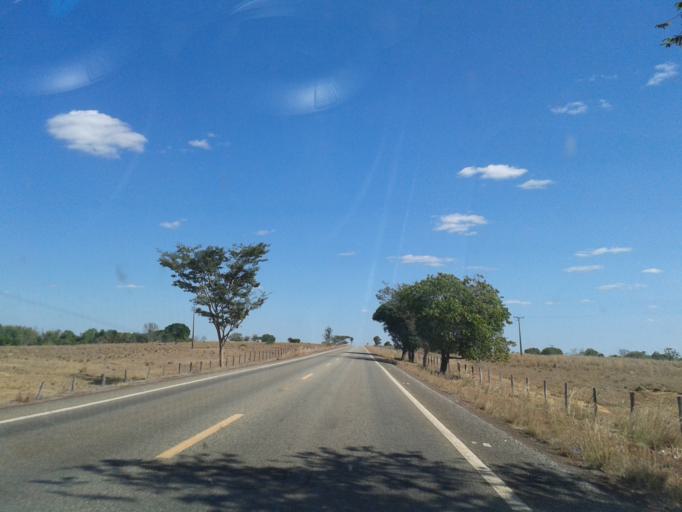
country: BR
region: Goias
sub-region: Sao Miguel Do Araguaia
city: Sao Miguel do Araguaia
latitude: -13.4108
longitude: -50.2660
